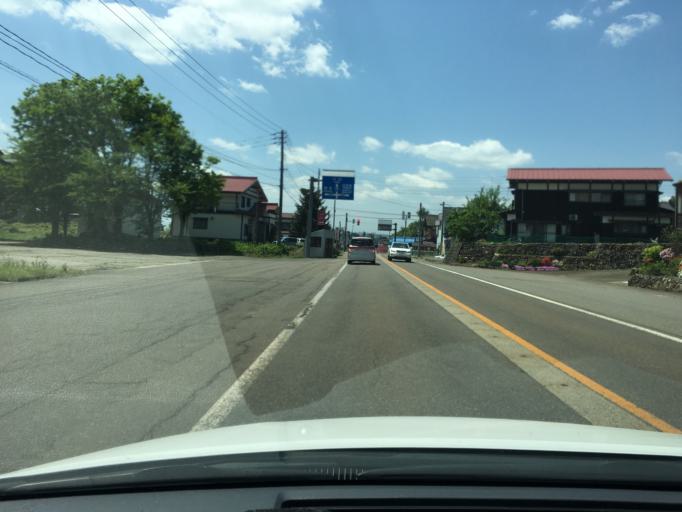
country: JP
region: Niigata
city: Ojiya
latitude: 37.2796
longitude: 138.9840
